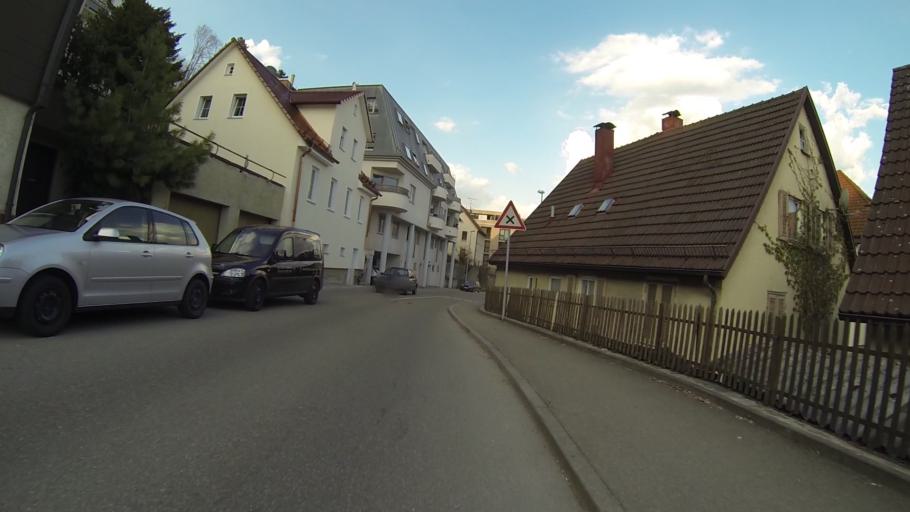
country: DE
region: Baden-Wuerttemberg
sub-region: Regierungsbezirk Stuttgart
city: Heidenheim an der Brenz
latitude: 48.6830
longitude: 10.1525
